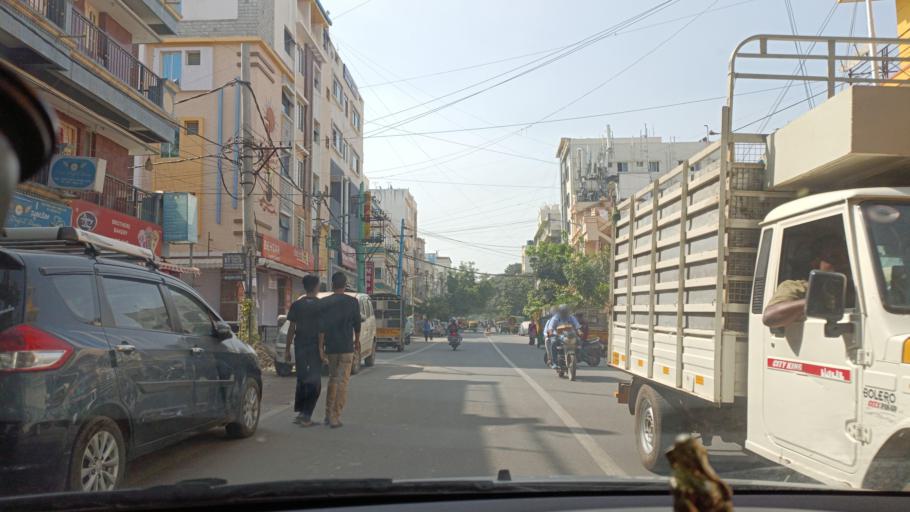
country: IN
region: Karnataka
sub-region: Bangalore Urban
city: Bangalore
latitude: 12.9194
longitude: 77.6166
